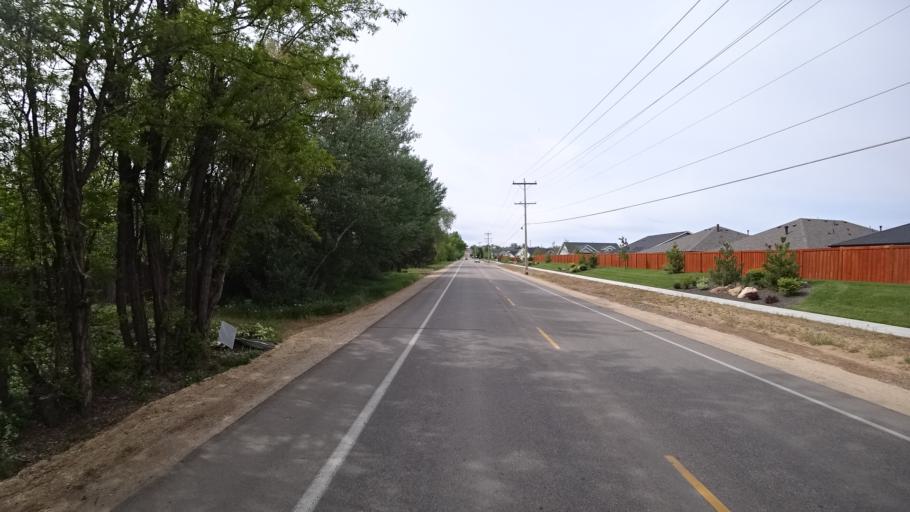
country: US
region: Idaho
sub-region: Ada County
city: Meridian
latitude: 43.5427
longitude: -116.3144
